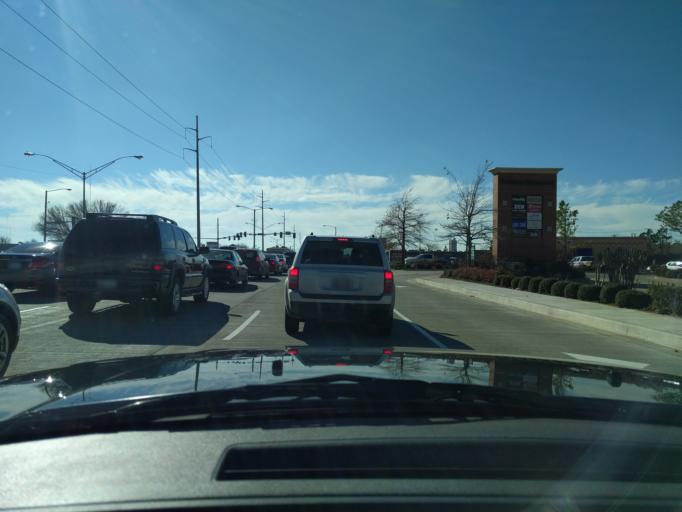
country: US
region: Oklahoma
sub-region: Oklahoma County
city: Edmond
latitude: 35.6246
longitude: -97.4860
